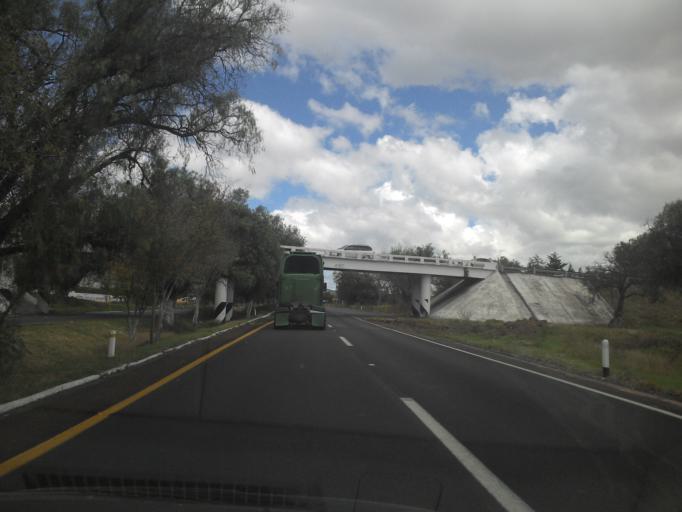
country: MX
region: Morelos
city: Teotihuacan de Arista
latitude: 19.6796
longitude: -98.8597
